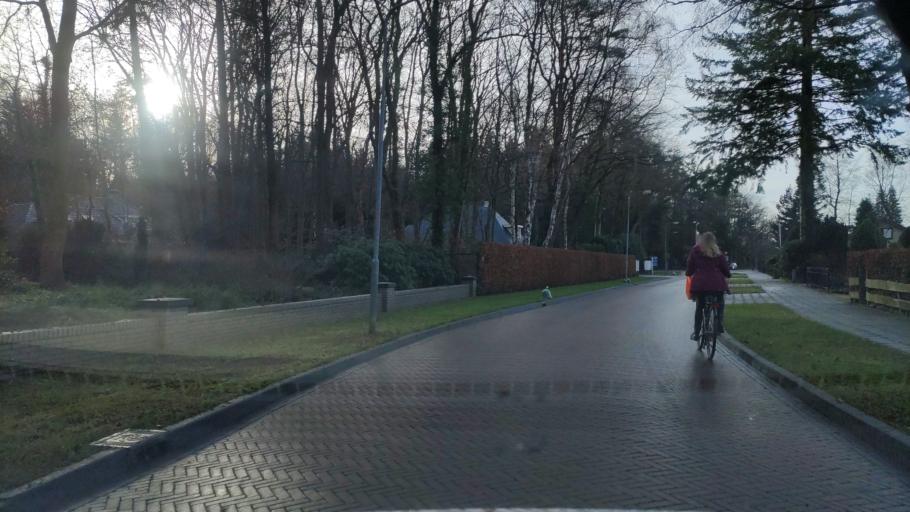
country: NL
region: Gelderland
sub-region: Gemeente Putten
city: Putten
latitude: 52.2555
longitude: 5.6196
